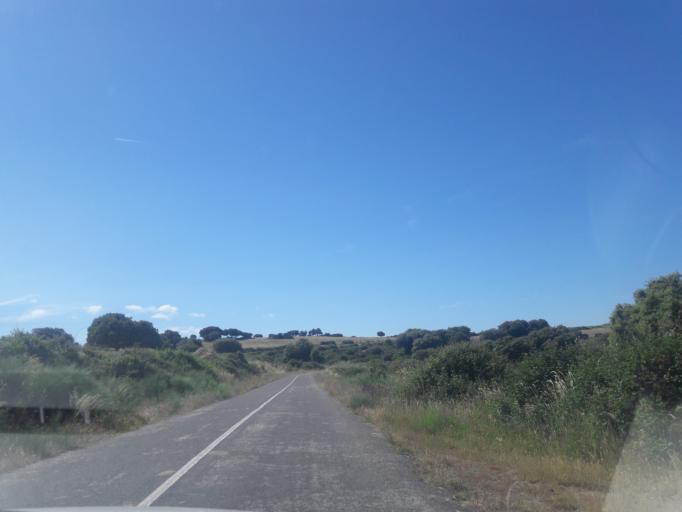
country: ES
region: Castille and Leon
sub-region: Provincia de Salamanca
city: Lumbrales
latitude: 40.9852
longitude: -6.7286
